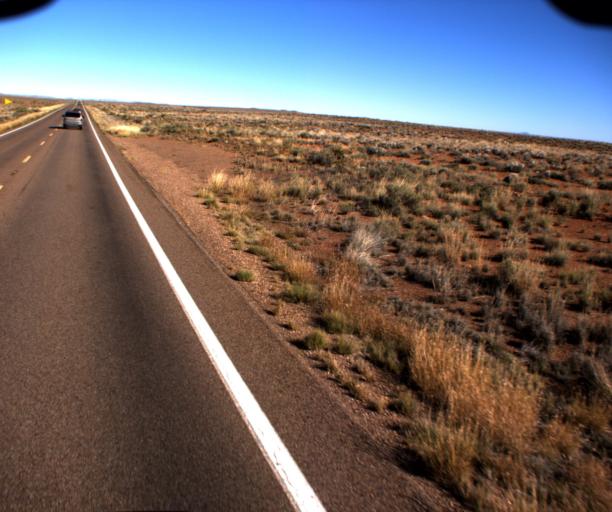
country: US
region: Arizona
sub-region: Navajo County
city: Holbrook
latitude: 34.7638
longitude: -110.1255
